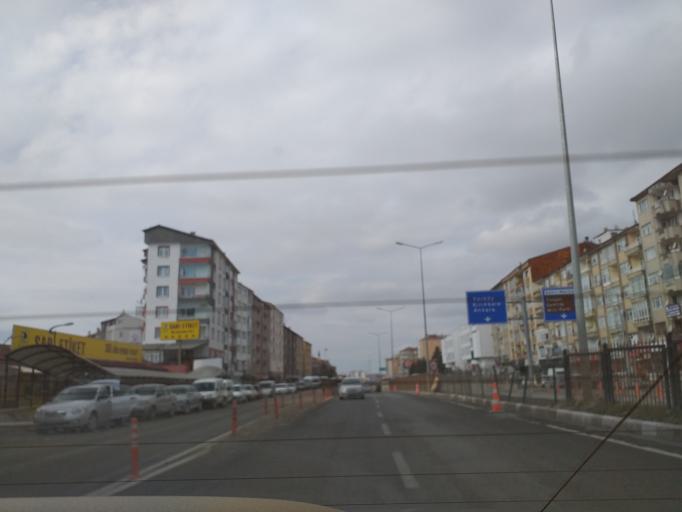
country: TR
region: Yozgat
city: Yozgat
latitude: 39.8219
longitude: 34.8129
